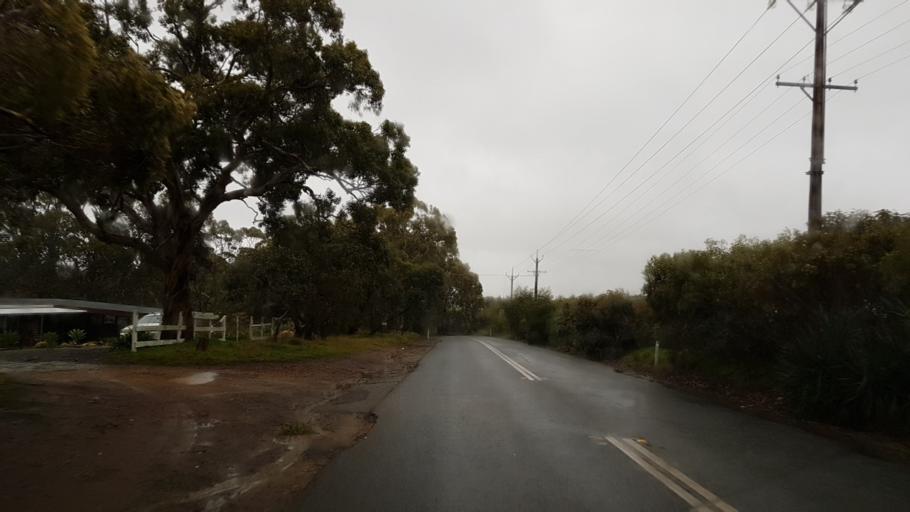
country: AU
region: South Australia
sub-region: Onkaparinga
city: Craigburn Farm
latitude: -35.0871
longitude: 138.6148
